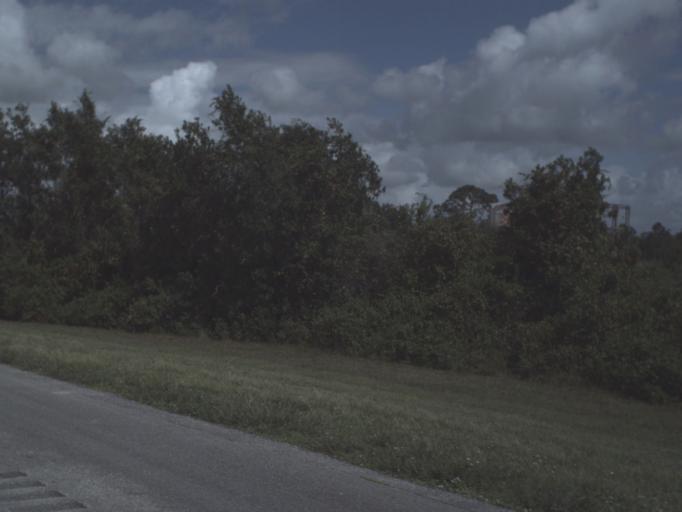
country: US
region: Florida
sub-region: Indian River County
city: Fellsmere
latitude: 27.6544
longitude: -80.8618
